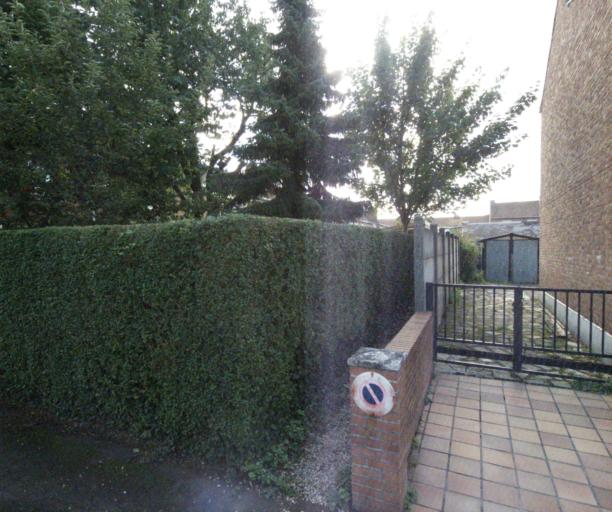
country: FR
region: Nord-Pas-de-Calais
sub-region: Departement du Nord
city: Loos
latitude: 50.6211
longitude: 3.0202
